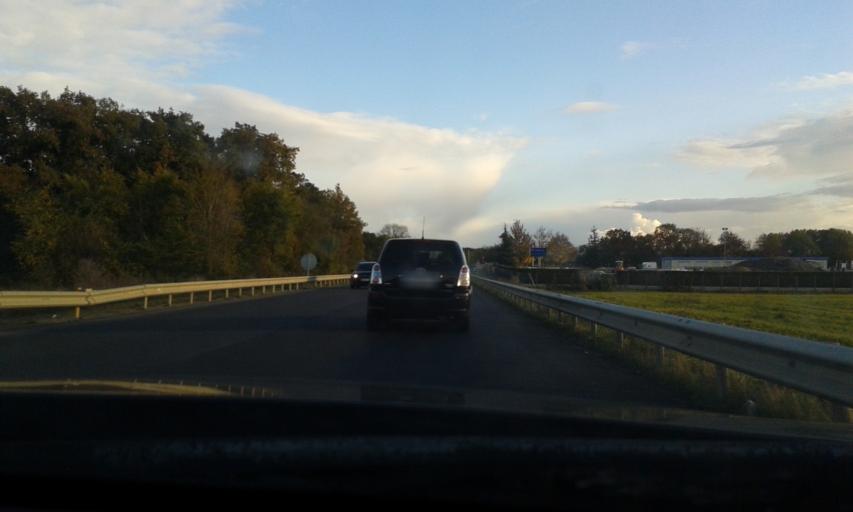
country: FR
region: Centre
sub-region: Departement d'Eure-et-Loir
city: Sours
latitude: 48.3936
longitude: 1.5650
